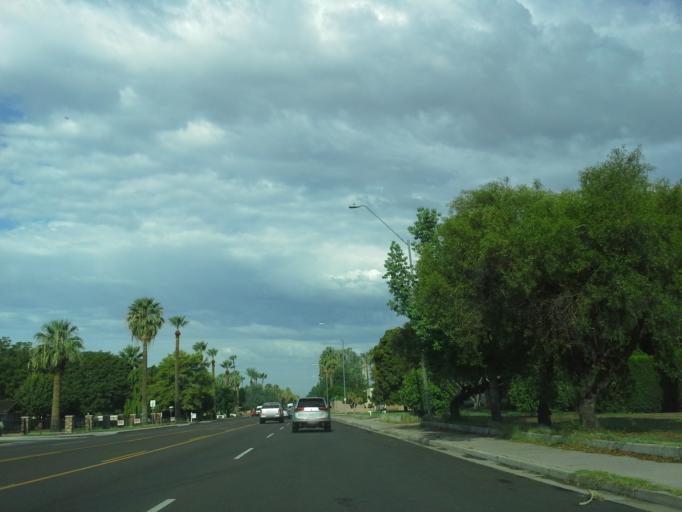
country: US
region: Arizona
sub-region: Maricopa County
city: Phoenix
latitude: 33.5384
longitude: -112.0666
